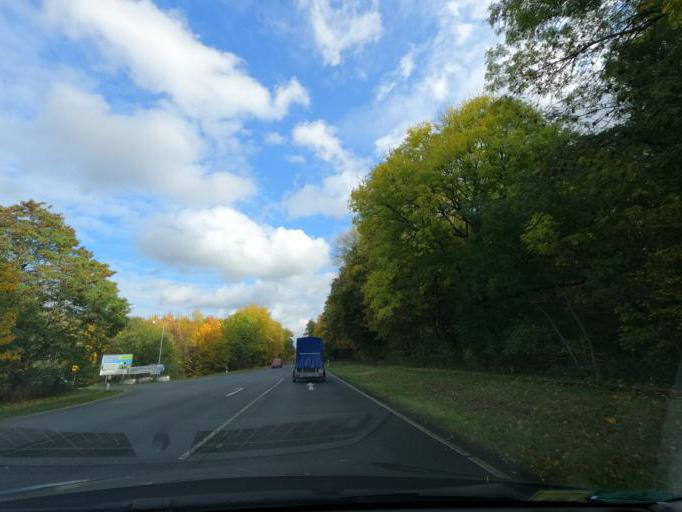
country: DE
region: Lower Saxony
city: Wolfenbuettel
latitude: 52.1533
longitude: 10.4977
